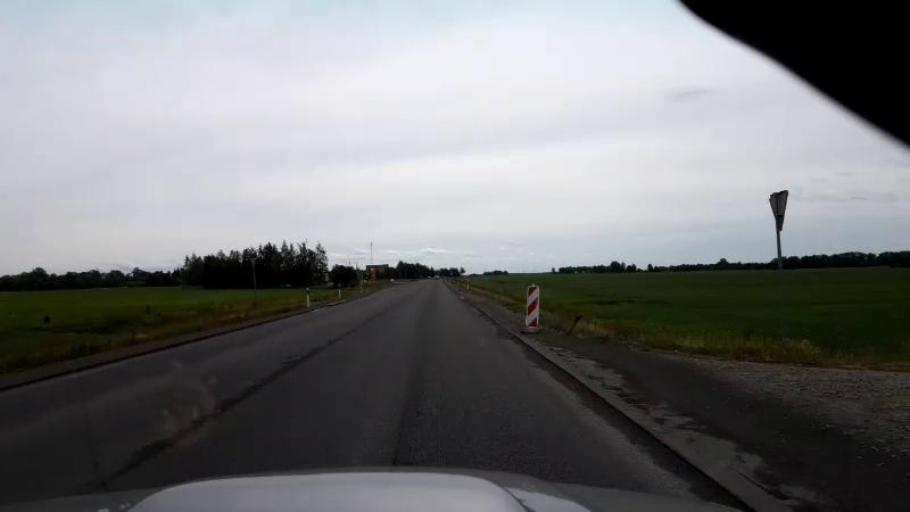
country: LV
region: Bauskas Rajons
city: Bauska
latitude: 56.3143
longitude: 24.3305
